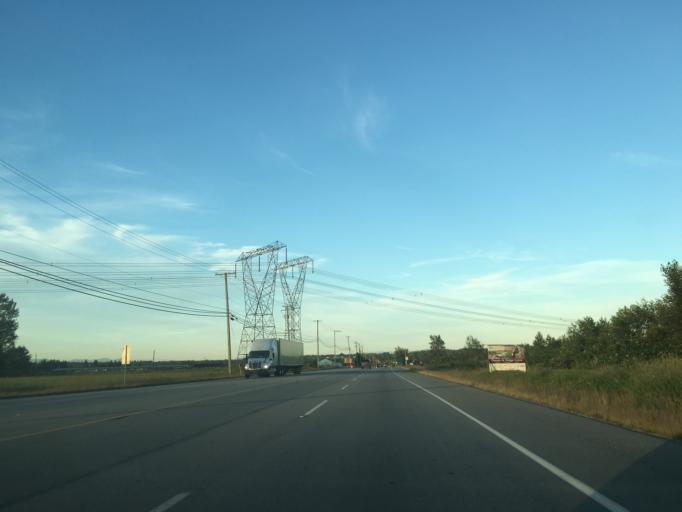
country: US
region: Washington
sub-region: Whatcom County
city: Blaine
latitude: 49.0165
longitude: -122.7447
